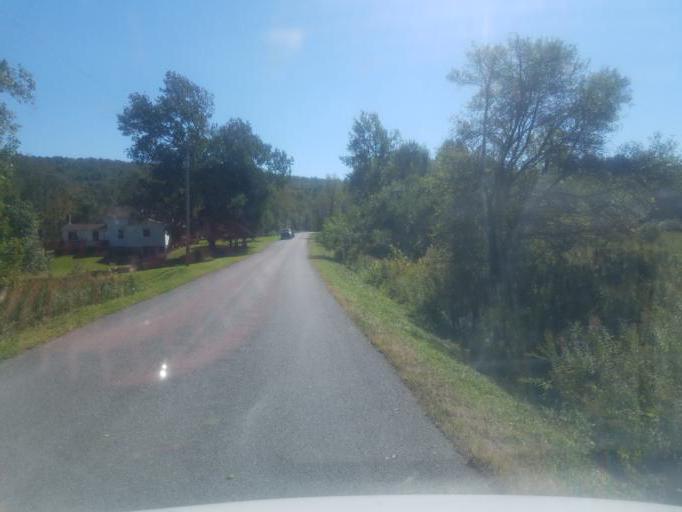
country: US
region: New York
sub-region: Allegany County
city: Houghton
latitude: 42.3246
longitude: -78.2028
